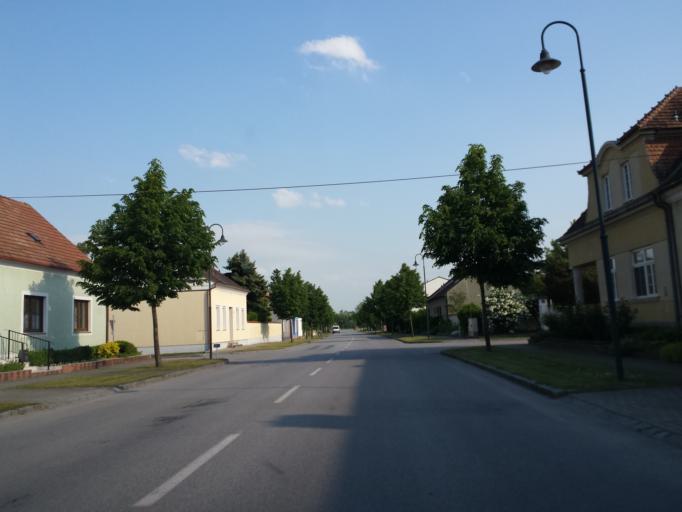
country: AT
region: Lower Austria
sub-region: Politischer Bezirk Ganserndorf
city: Marchegg
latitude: 48.3056
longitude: 16.8729
